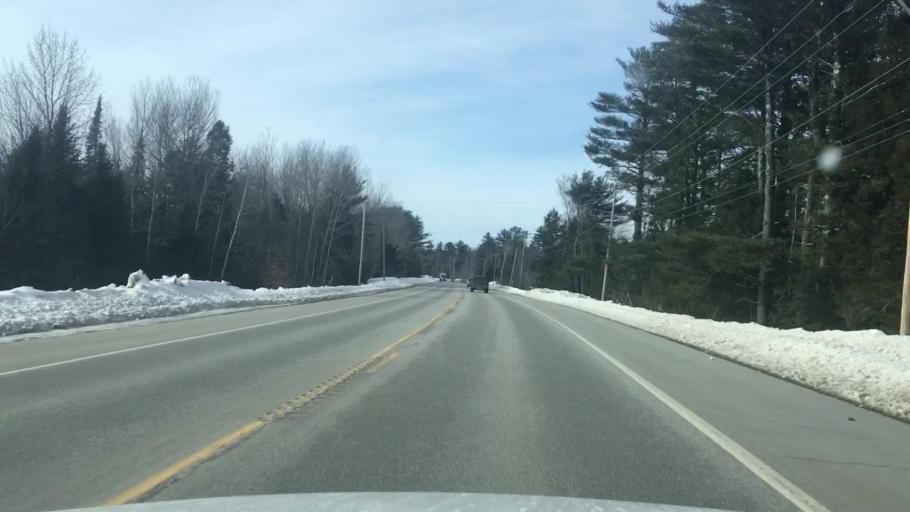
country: US
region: Maine
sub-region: Penobscot County
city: Kenduskeag
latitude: 44.9595
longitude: -68.9553
